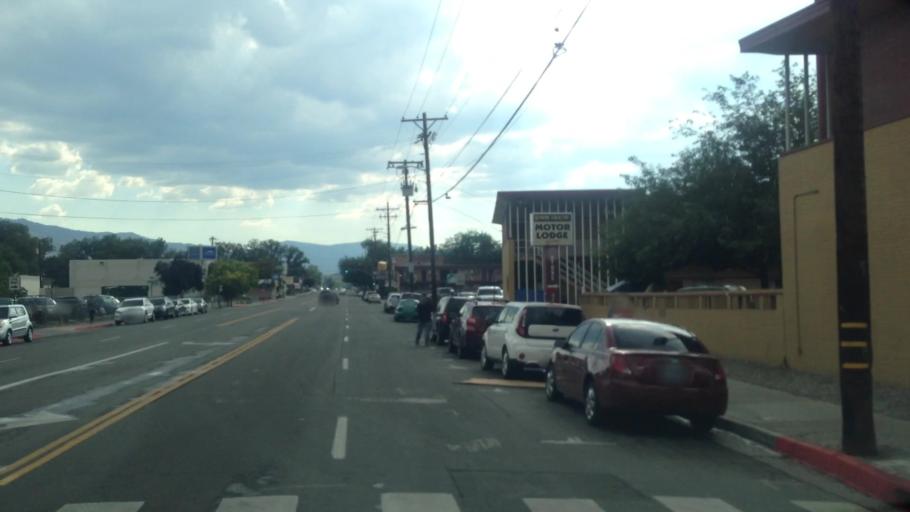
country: US
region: Nevada
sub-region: Washoe County
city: Reno
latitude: 39.5262
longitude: -119.8173
